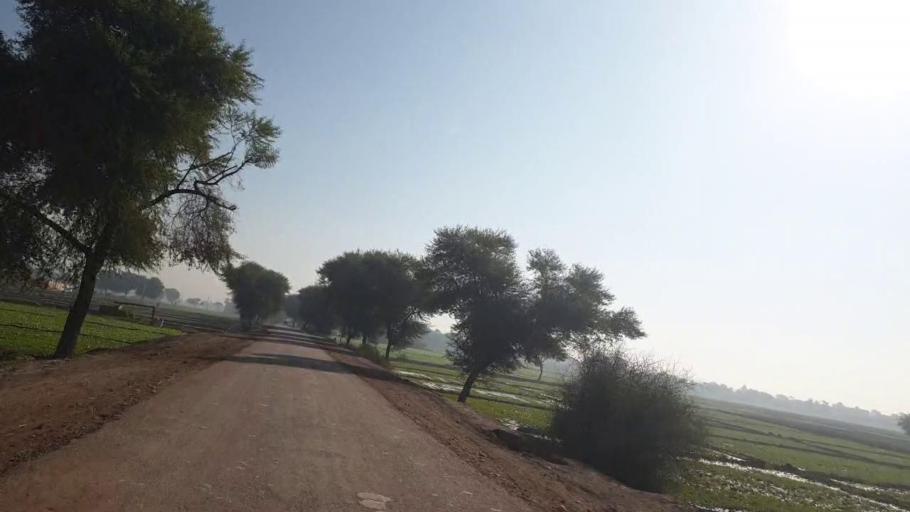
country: PK
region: Sindh
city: Dadu
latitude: 26.6706
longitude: 67.8479
